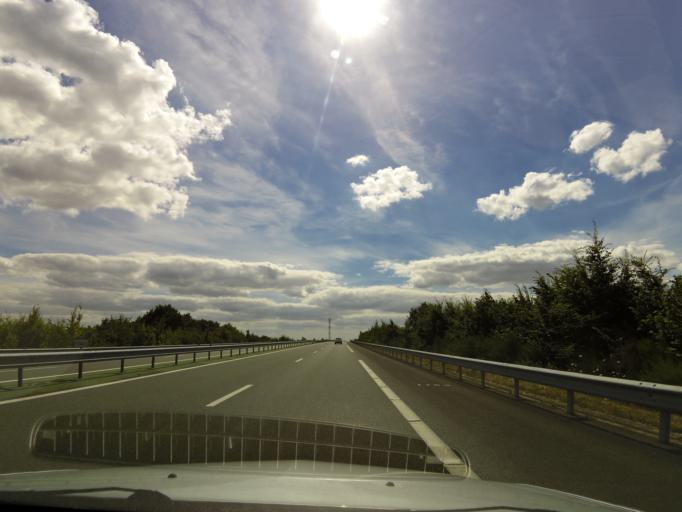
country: FR
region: Pays de la Loire
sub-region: Departement de la Vendee
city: La Ferriere
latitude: 46.6825
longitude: -1.3294
